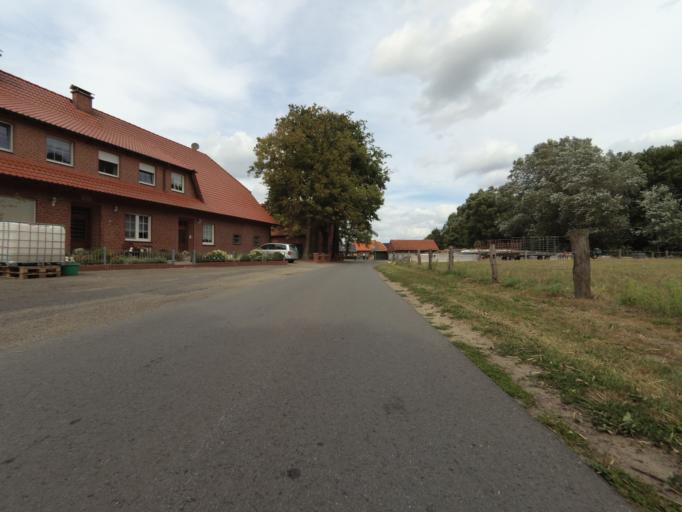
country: DE
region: North Rhine-Westphalia
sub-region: Regierungsbezirk Munster
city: Ahaus
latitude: 52.1178
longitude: 7.0149
